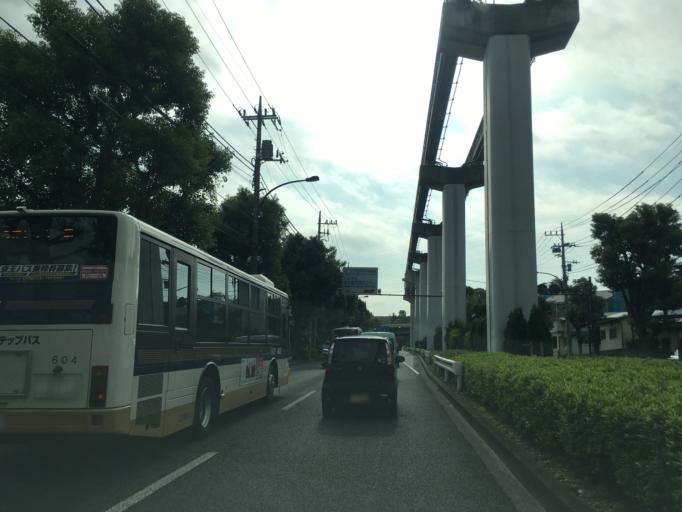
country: JP
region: Tokyo
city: Hino
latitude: 35.6351
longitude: 139.4193
